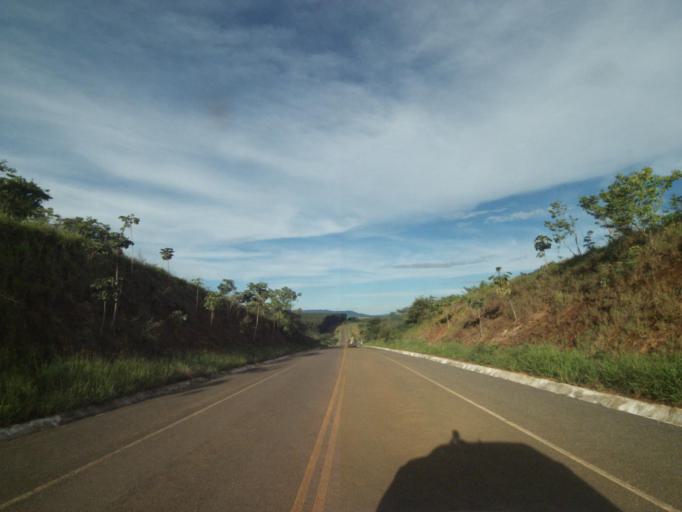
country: BR
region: Goias
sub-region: Jaragua
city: Jaragua
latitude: -15.8858
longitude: -49.4519
